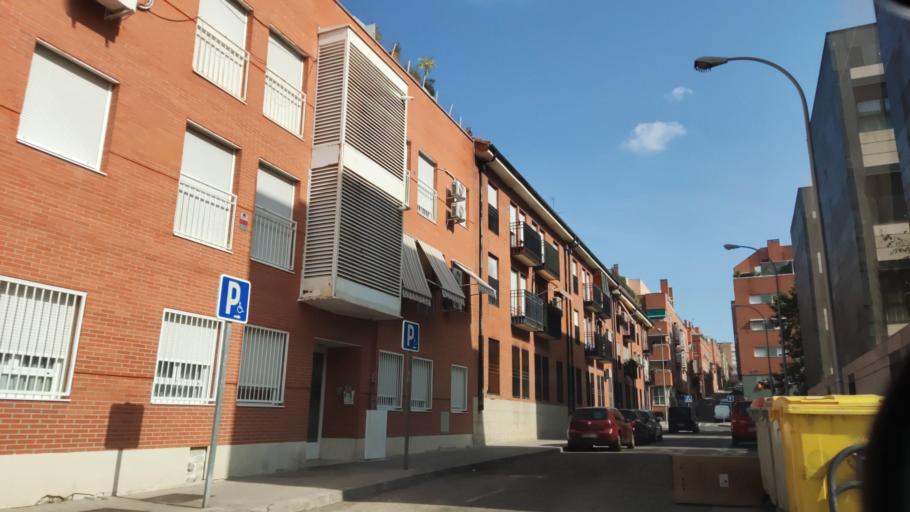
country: ES
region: Madrid
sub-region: Provincia de Madrid
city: Chamartin
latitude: 40.4728
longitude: -3.6950
